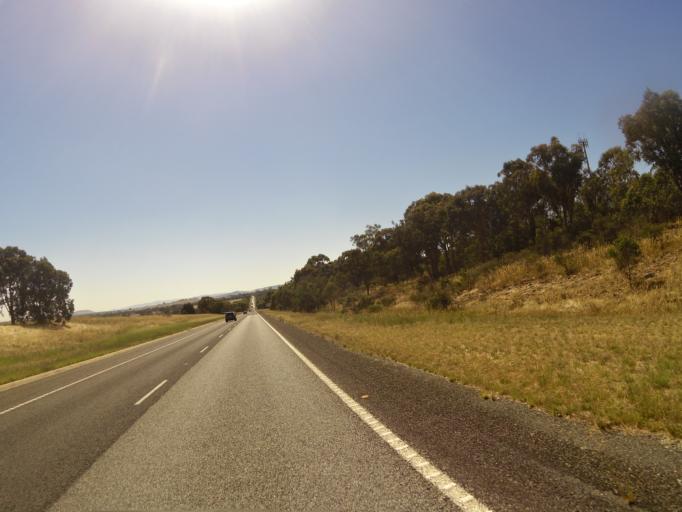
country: AU
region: Victoria
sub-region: Greater Shepparton
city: Shepparton
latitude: -36.8315
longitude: 145.3929
